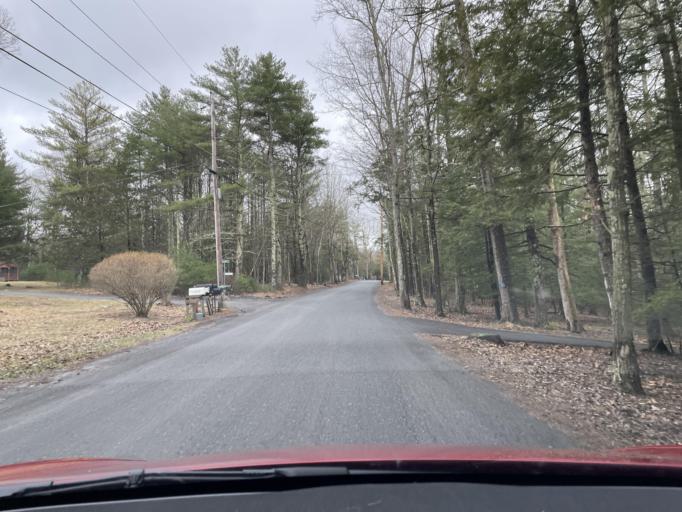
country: US
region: New York
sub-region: Ulster County
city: Manorville
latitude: 42.0942
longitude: -74.0355
